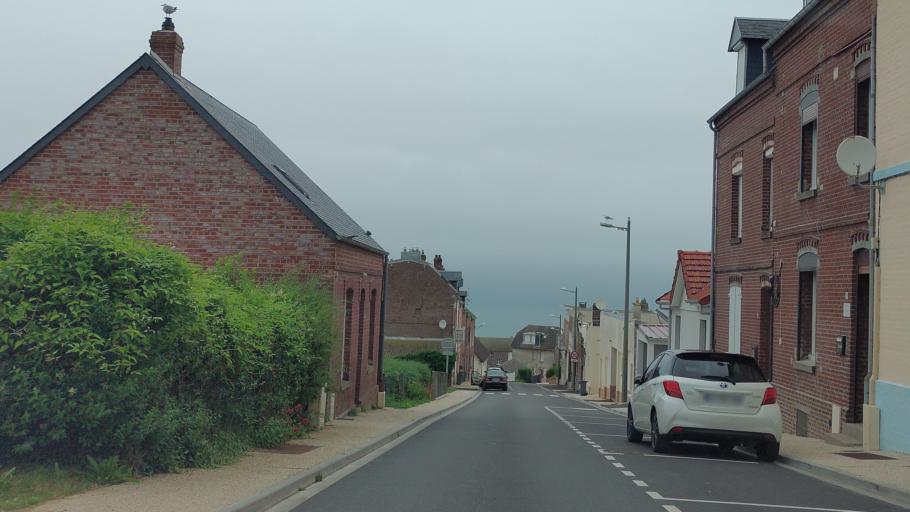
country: FR
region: Picardie
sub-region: Departement de la Somme
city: Ault
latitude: 50.1039
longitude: 1.4521
